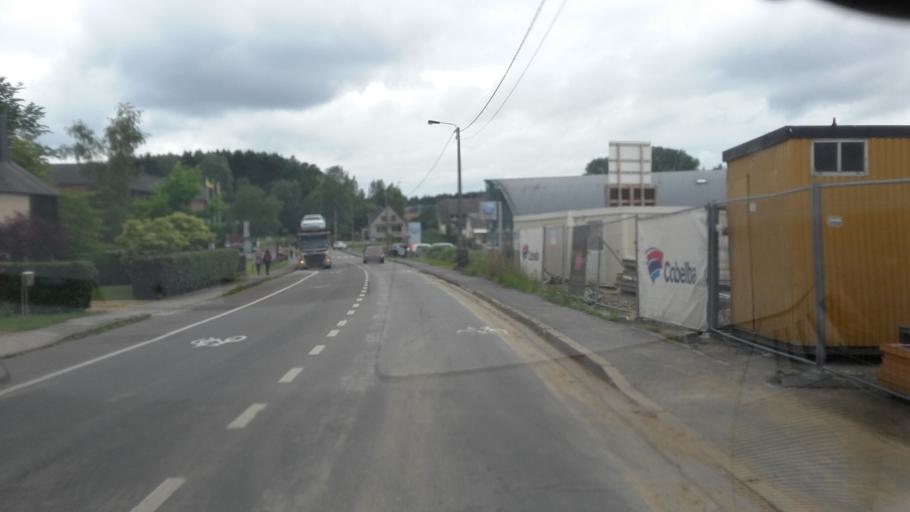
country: BE
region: Wallonia
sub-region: Province du Luxembourg
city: Arlon
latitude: 49.6842
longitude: 5.7968
